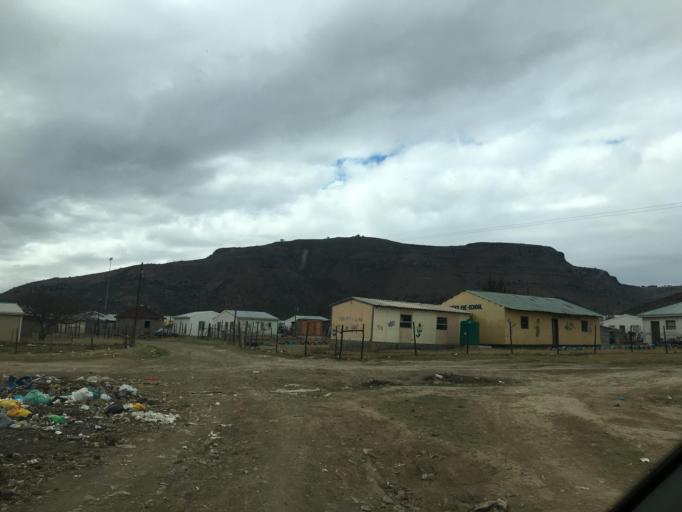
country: ZA
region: Eastern Cape
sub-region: Chris Hani District Municipality
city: Cala
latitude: -31.5359
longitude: 27.6997
